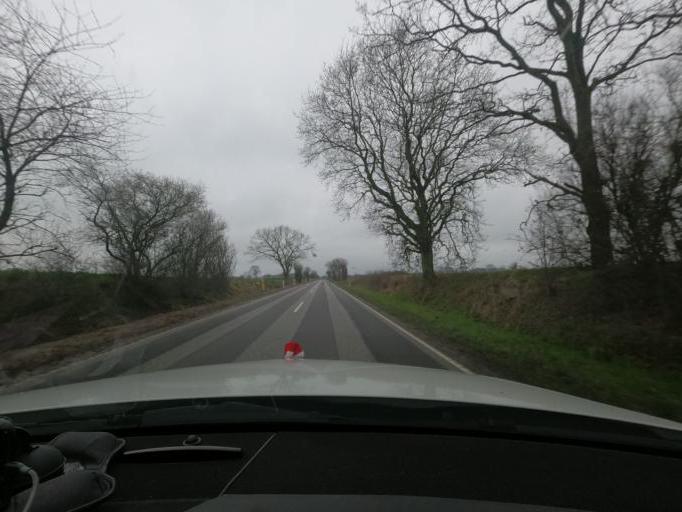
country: DK
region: South Denmark
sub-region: Haderslev Kommune
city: Starup
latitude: 55.2274
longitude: 9.6321
